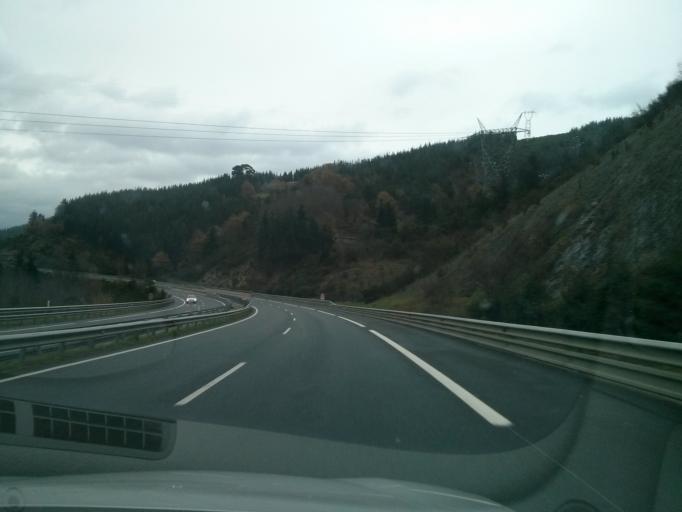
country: ES
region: Basque Country
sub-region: Bizkaia
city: Alonsotegi
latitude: 43.2153
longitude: -3.0290
